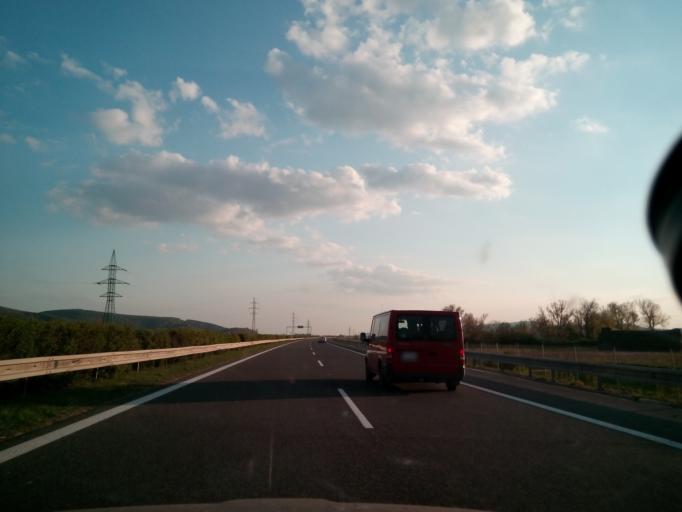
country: SK
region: Trenciansky
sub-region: Okres Trencin
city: Trencin
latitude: 48.8430
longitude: 17.9421
